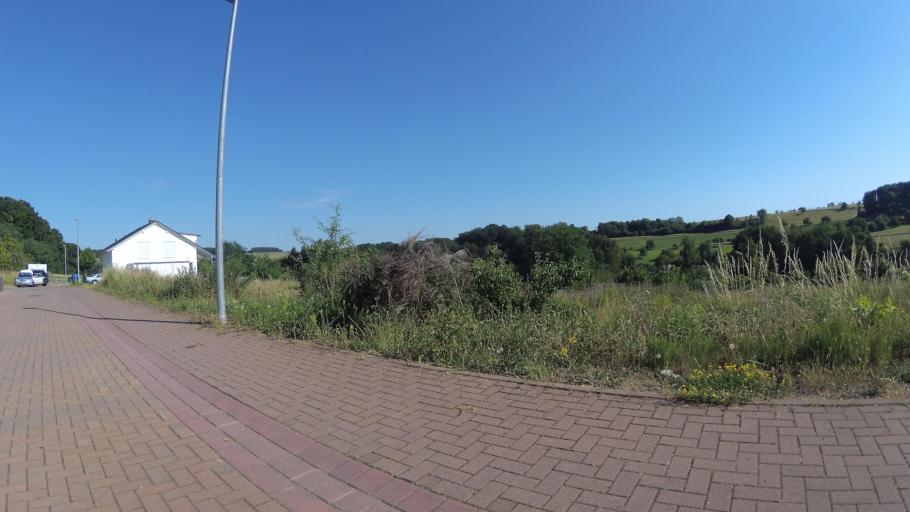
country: DE
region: Rheinland-Pfalz
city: Althornbach
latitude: 49.2144
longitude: 7.3255
